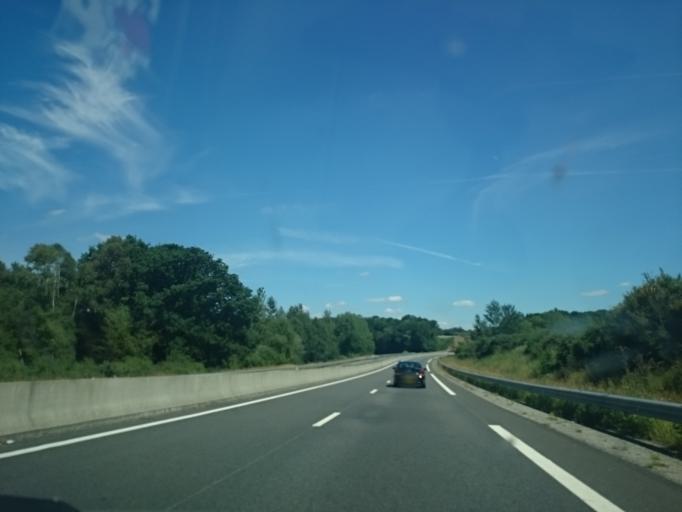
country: FR
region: Brittany
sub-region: Departement des Cotes-d'Armor
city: Gouarec
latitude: 48.2279
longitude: -3.1150
